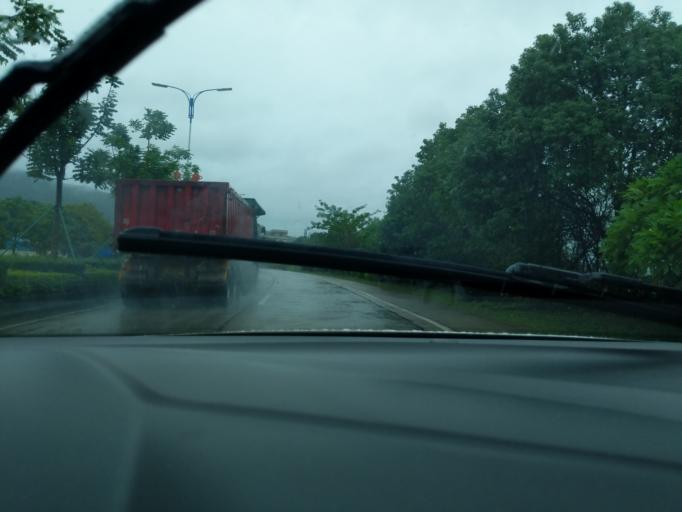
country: CN
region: Guangdong
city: Pingshi
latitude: 22.2111
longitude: 112.3239
